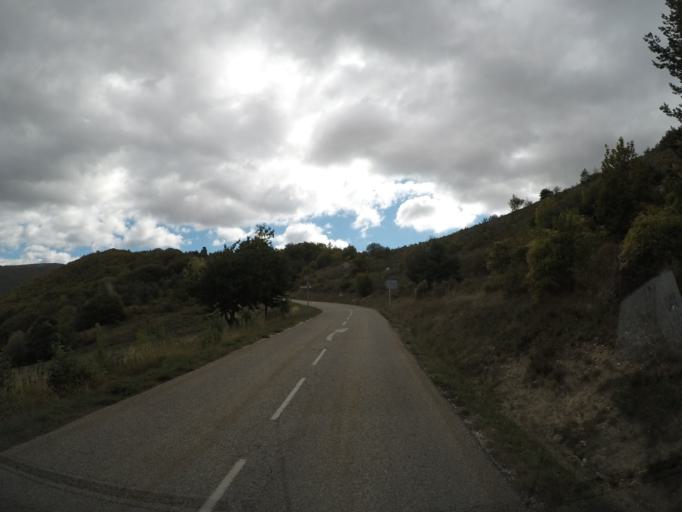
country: FR
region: Provence-Alpes-Cote d'Azur
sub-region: Departement du Vaucluse
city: Sault
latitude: 44.1834
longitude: 5.5086
